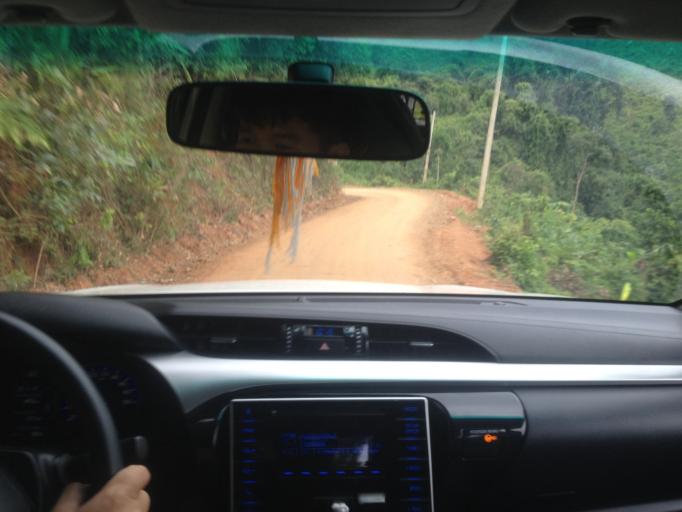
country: TH
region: Nan
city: Chaloem Phra Kiat
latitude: 19.9708
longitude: 101.1362
